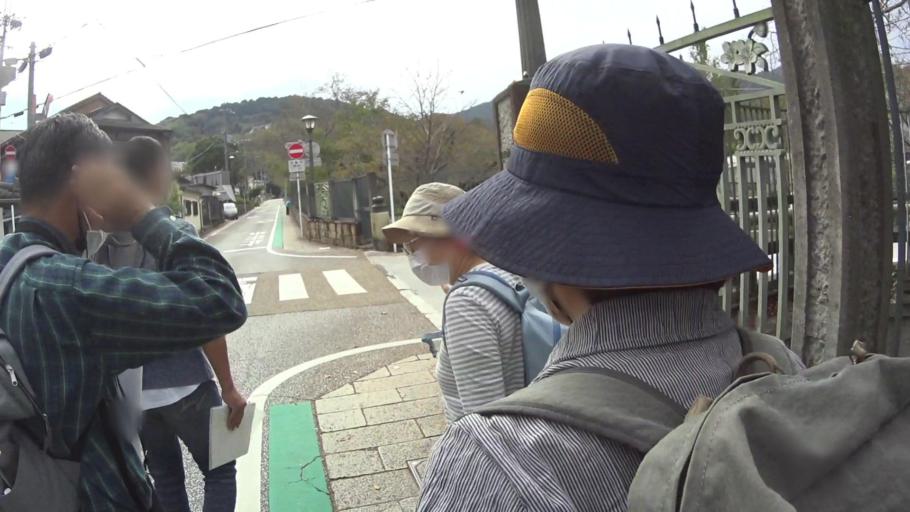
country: JP
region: Shiga Prefecture
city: Hikone
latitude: 35.2705
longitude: 136.3742
